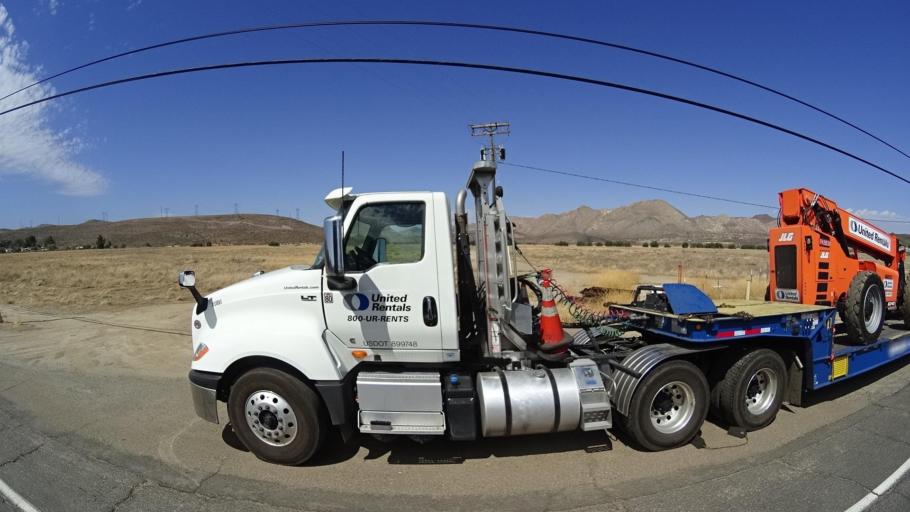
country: MX
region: Baja California
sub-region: Tecate
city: Cereso del Hongo
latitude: 32.6176
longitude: -116.1786
